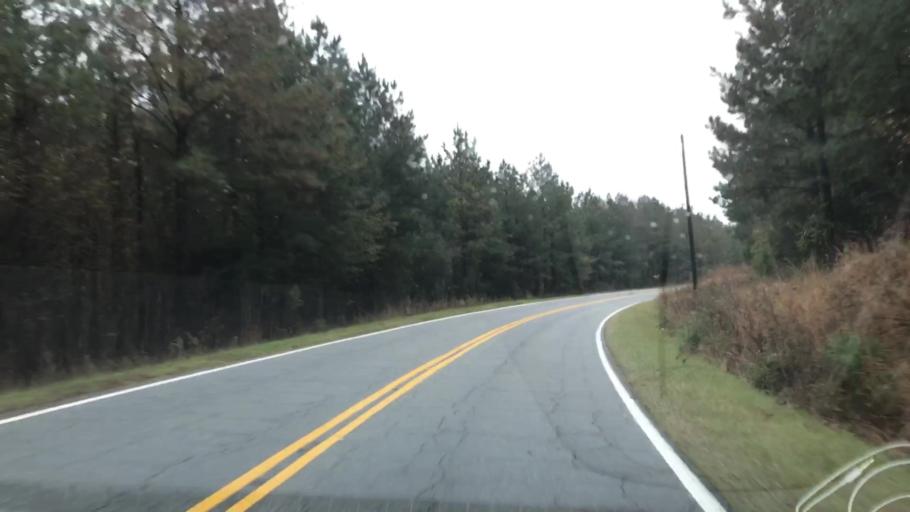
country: US
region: South Carolina
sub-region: Laurens County
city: Joanna
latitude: 34.3681
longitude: -81.7805
